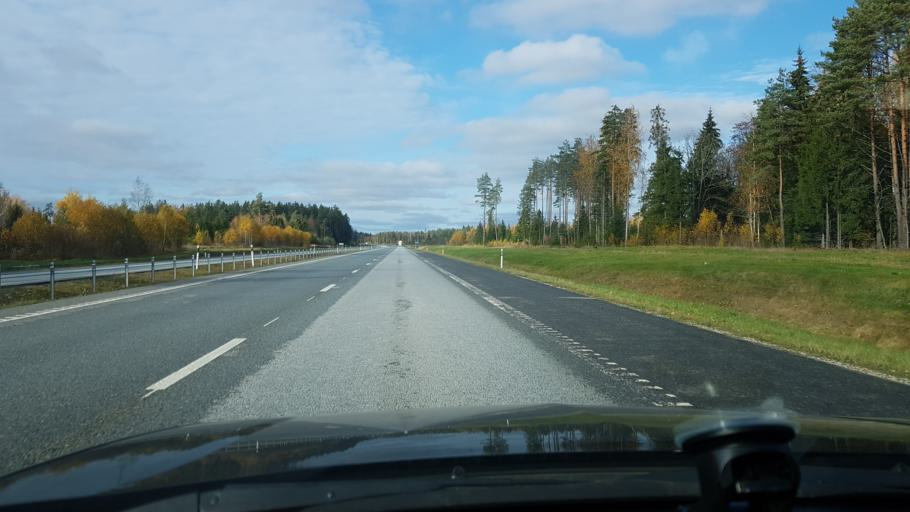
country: EE
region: Laeaene-Virumaa
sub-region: Kadrina vald
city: Kadrina
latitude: 59.4570
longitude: 26.0440
